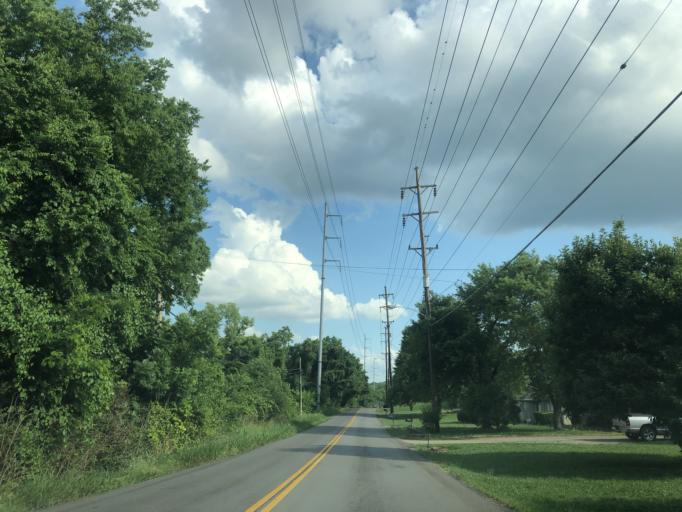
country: US
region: Tennessee
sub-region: Davidson County
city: Nashville
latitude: 36.2270
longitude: -86.8232
